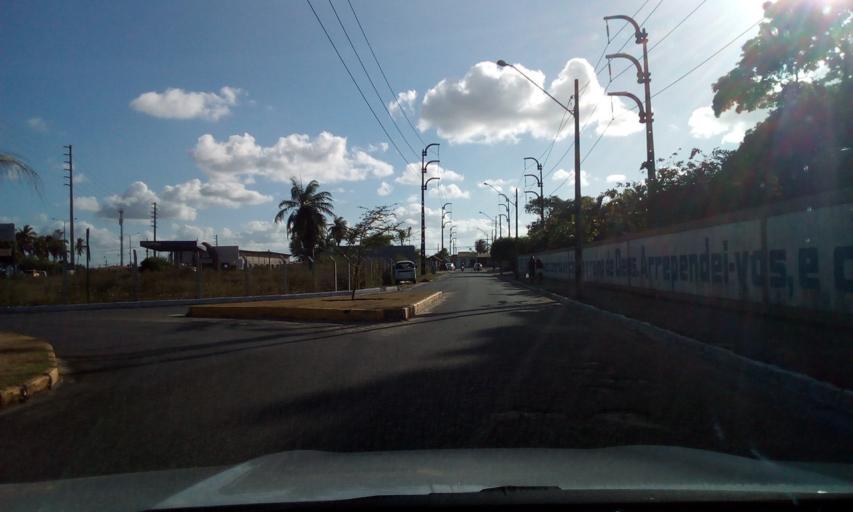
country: BR
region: Paraiba
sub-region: Bayeux
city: Bayeux
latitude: -7.1451
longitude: -34.9081
